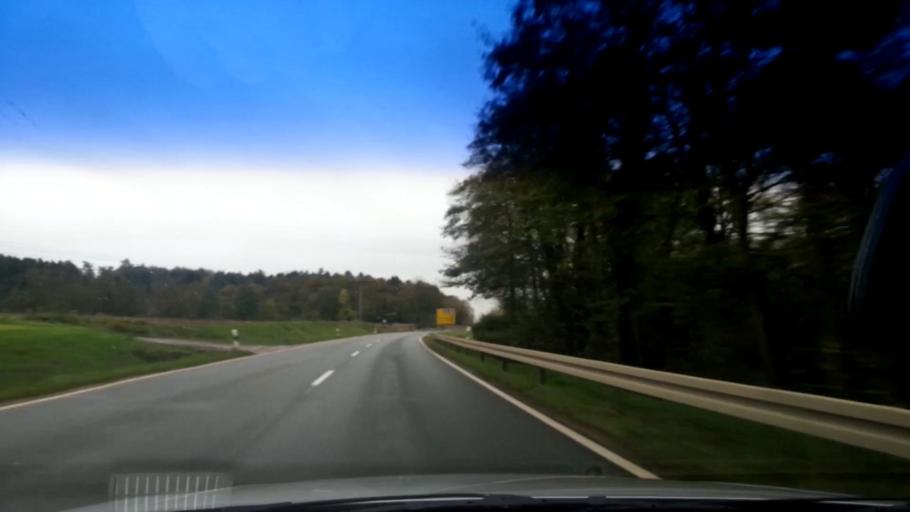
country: DE
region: Bavaria
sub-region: Upper Franconia
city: Schesslitz
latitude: 50.0042
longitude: 11.0666
